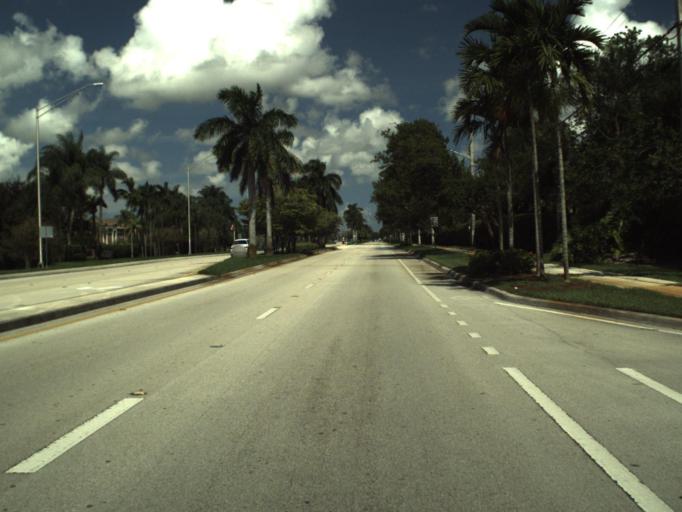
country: US
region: Florida
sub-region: Miami-Dade County
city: Country Club
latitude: 25.9932
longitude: -80.3075
